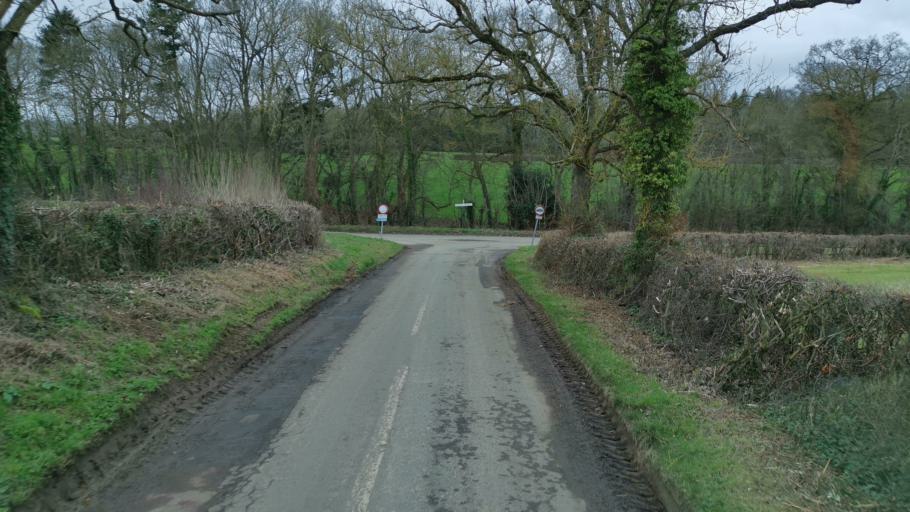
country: GB
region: England
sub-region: Oxfordshire
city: Somerton
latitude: 51.9041
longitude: -1.3173
